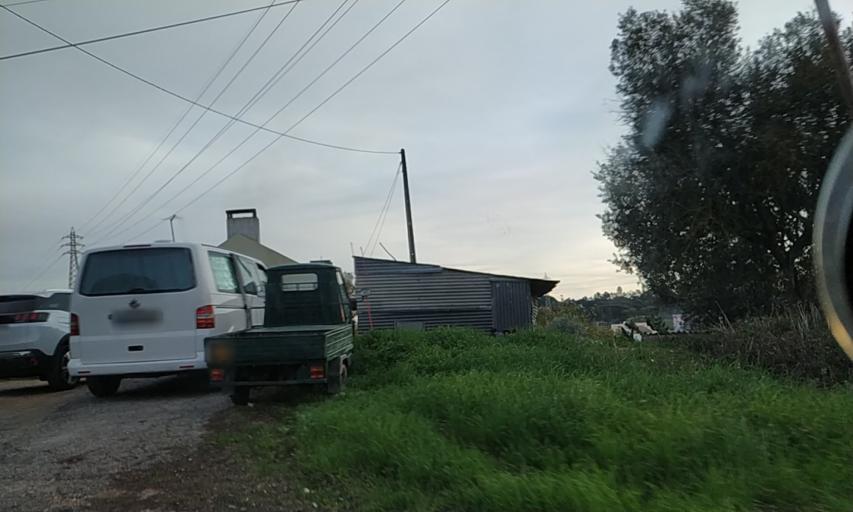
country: PT
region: Setubal
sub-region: Setubal
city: Setubal
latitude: 38.5259
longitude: -8.8568
